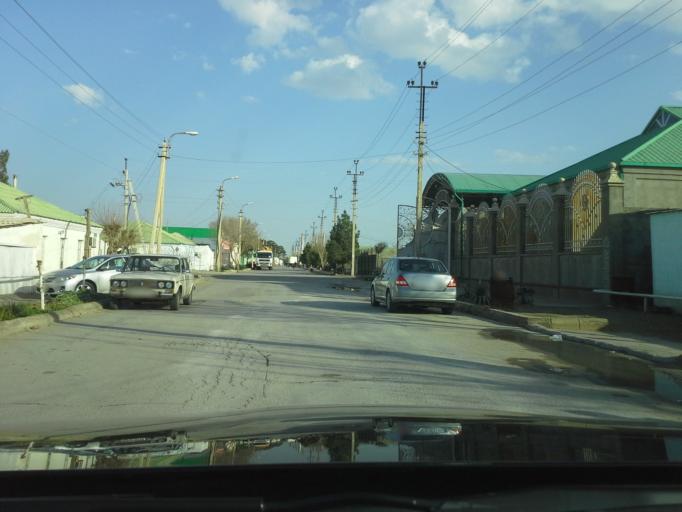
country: TM
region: Ahal
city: Abadan
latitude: 38.0266
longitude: 58.2353
